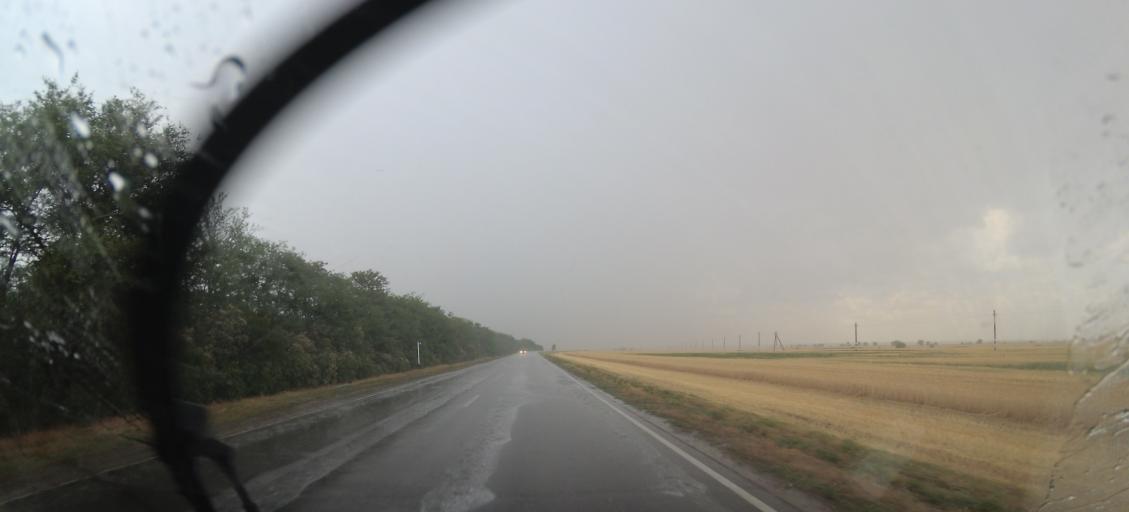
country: RU
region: Rostov
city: Proletarsk
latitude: 46.6677
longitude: 41.6907
